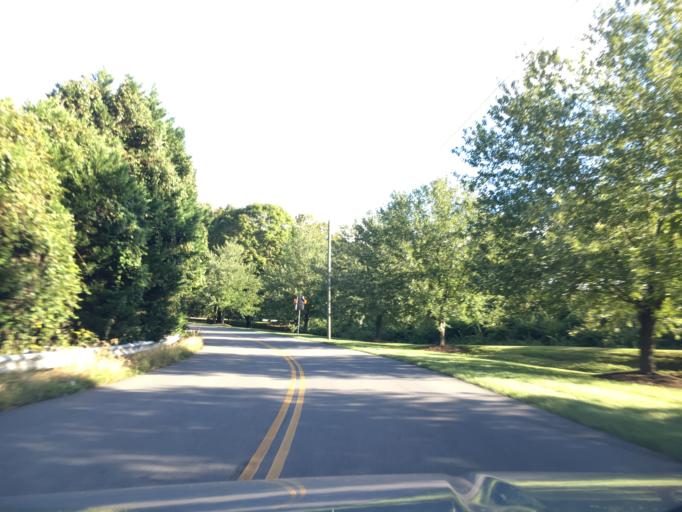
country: US
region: Virginia
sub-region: City of Lynchburg
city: West Lynchburg
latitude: 37.3888
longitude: -79.1603
